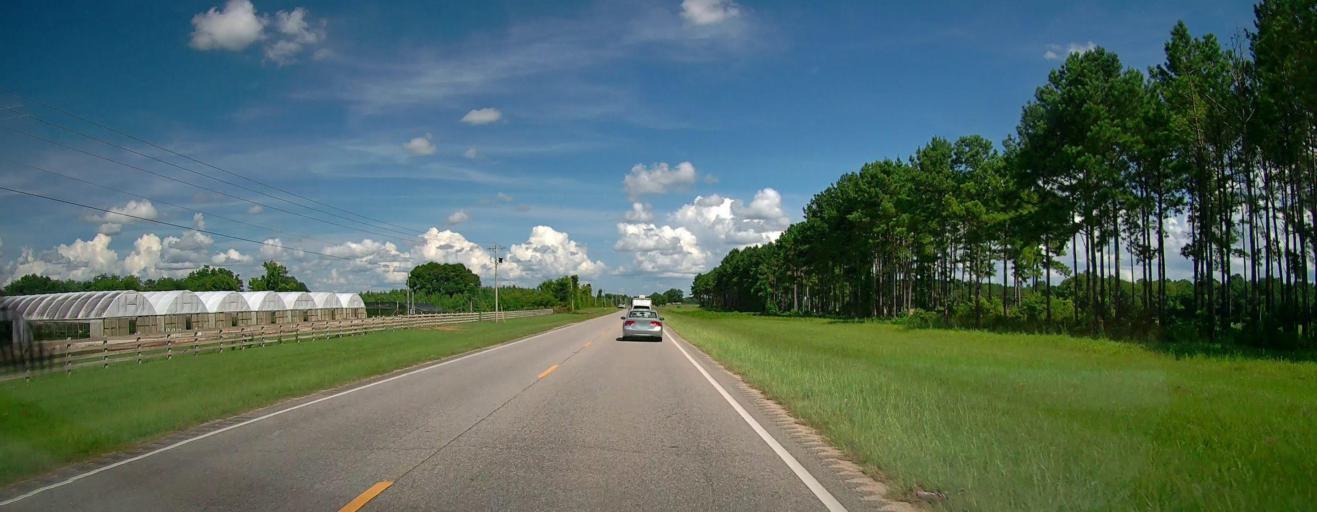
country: US
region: Alabama
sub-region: Elmore County
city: Tallassee
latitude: 32.3911
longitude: -85.8966
